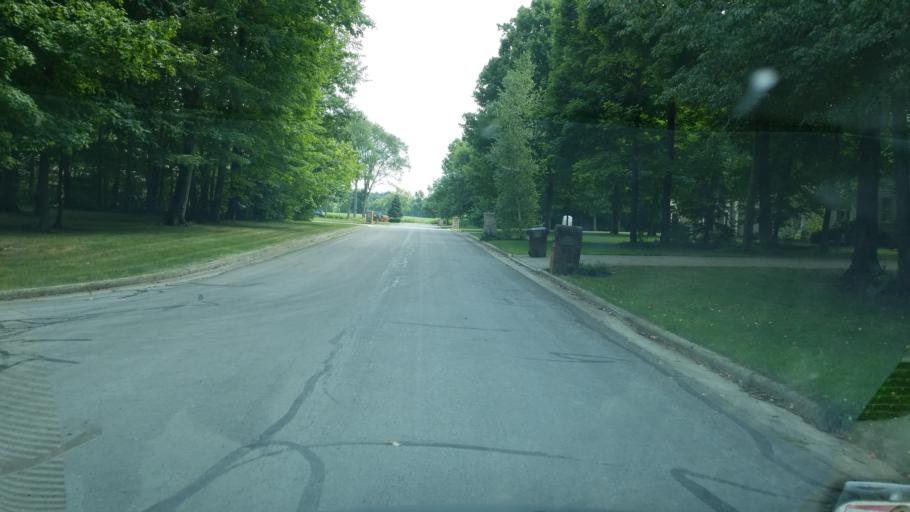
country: US
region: Ohio
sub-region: Marion County
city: Marion
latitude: 40.5299
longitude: -83.0878
